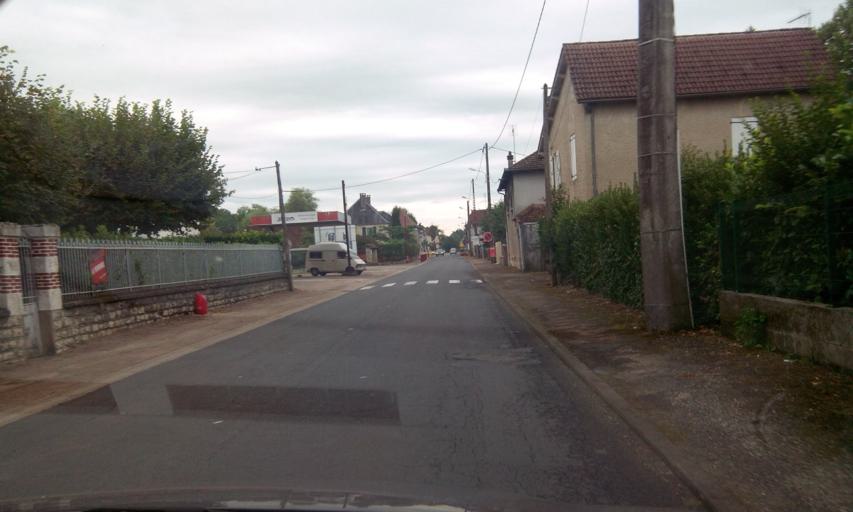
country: FR
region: Midi-Pyrenees
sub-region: Departement du Lot
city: Vayrac
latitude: 44.9445
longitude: 1.7305
